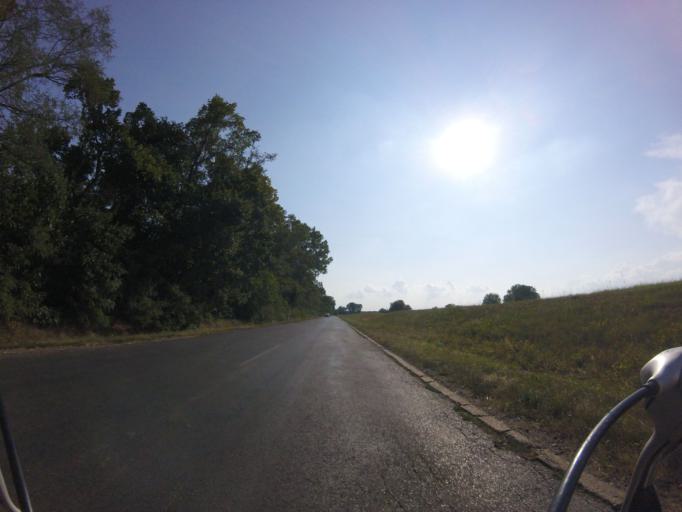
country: HU
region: Szabolcs-Szatmar-Bereg
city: Kek
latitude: 48.1024
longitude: 21.8997
